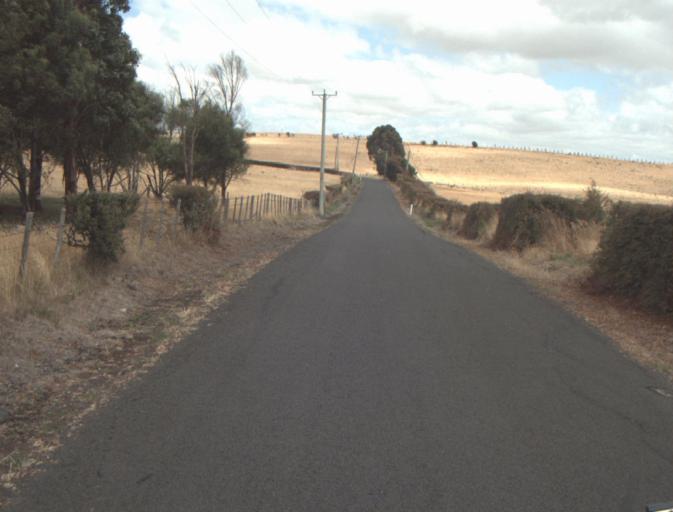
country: AU
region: Tasmania
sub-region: Northern Midlands
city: Evandale
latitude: -41.5084
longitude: 147.2518
